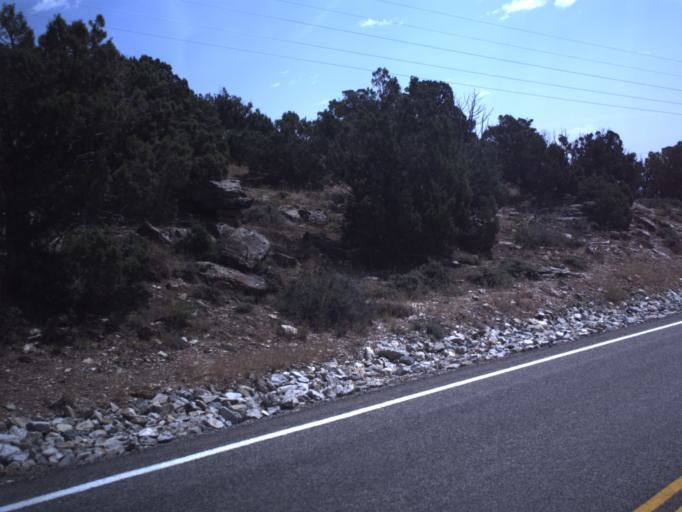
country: US
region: Utah
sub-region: Uintah County
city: Vernal
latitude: 40.6386
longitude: -109.4808
